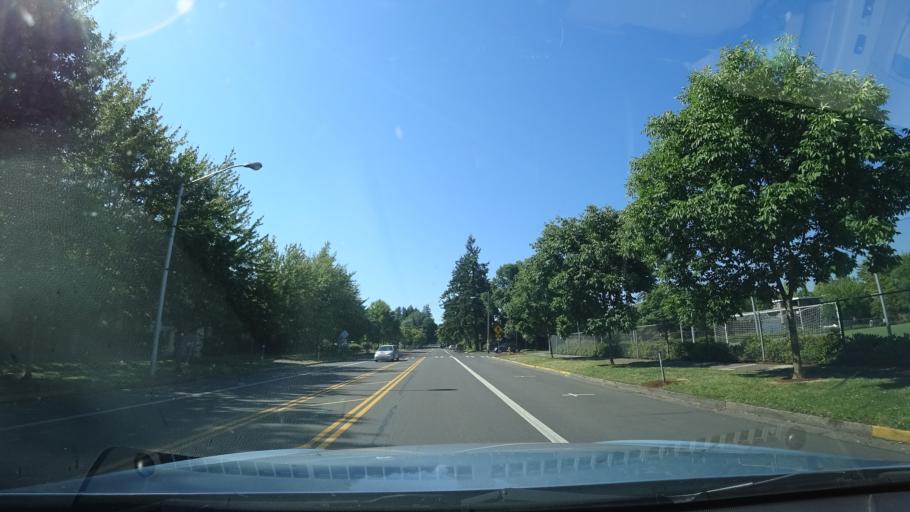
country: US
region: Oregon
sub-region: Lane County
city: Eugene
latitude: 44.0406
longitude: -123.0697
